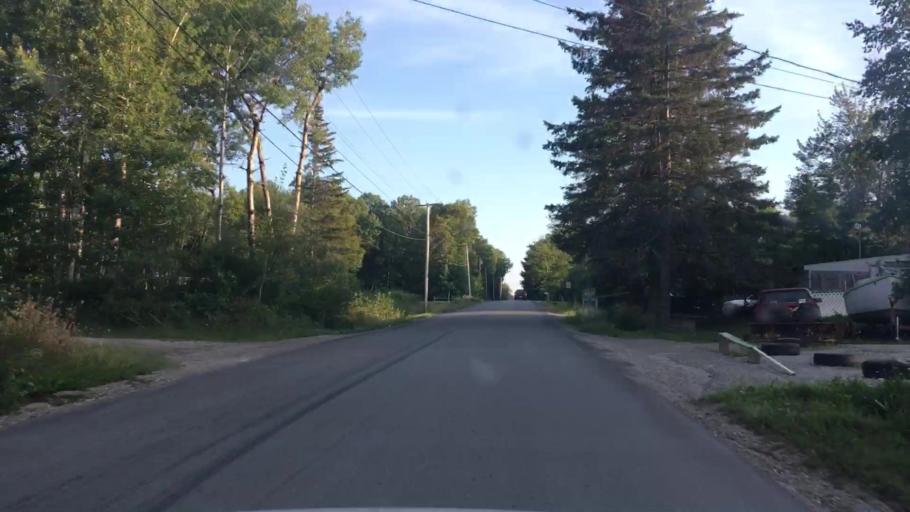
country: US
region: Maine
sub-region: Penobscot County
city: Hampden
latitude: 44.7193
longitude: -68.8870
